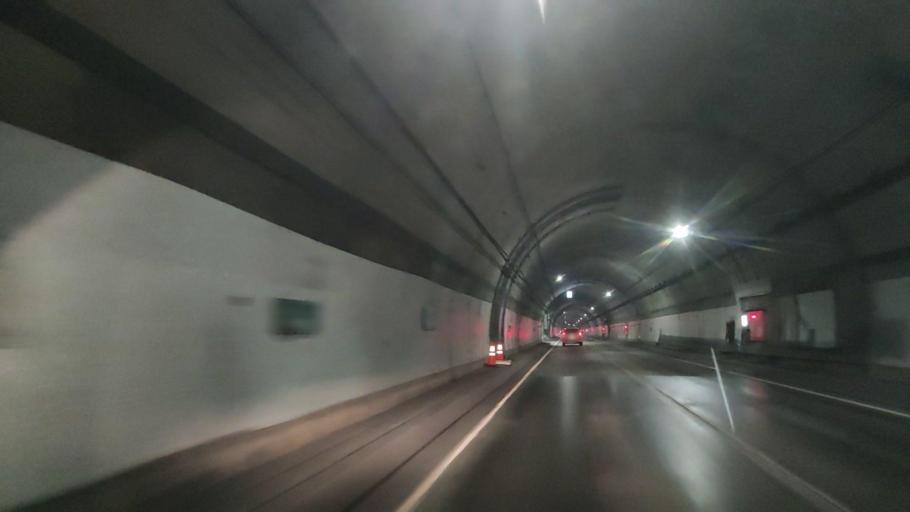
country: JP
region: Hokkaido
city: Rumoi
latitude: 43.7055
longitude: 141.3350
